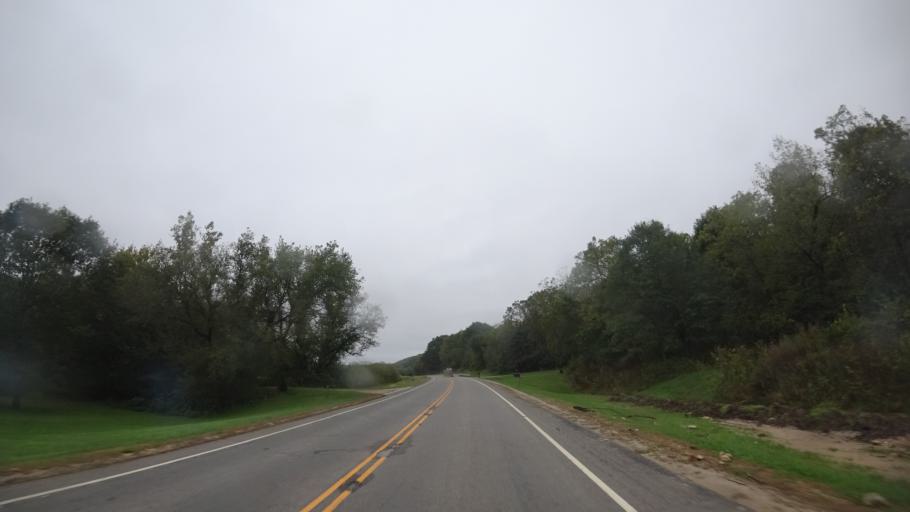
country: US
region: Wisconsin
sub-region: Crawford County
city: Prairie du Chien
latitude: 43.0508
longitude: -90.9803
